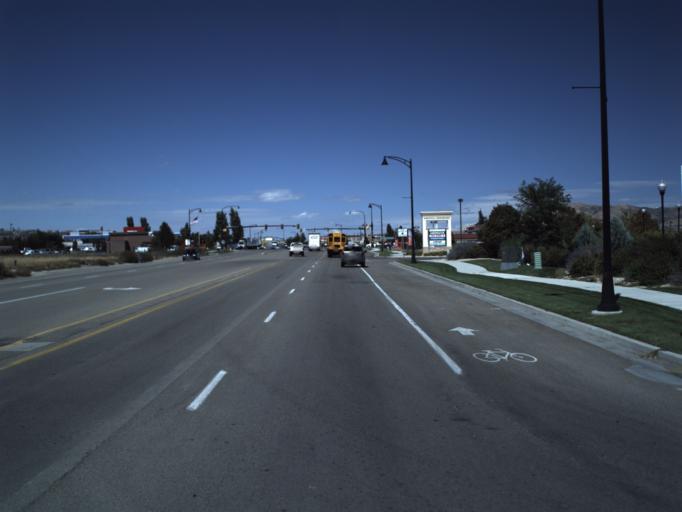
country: US
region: Utah
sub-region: Utah County
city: Saratoga Springs
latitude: 40.3849
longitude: -111.9163
